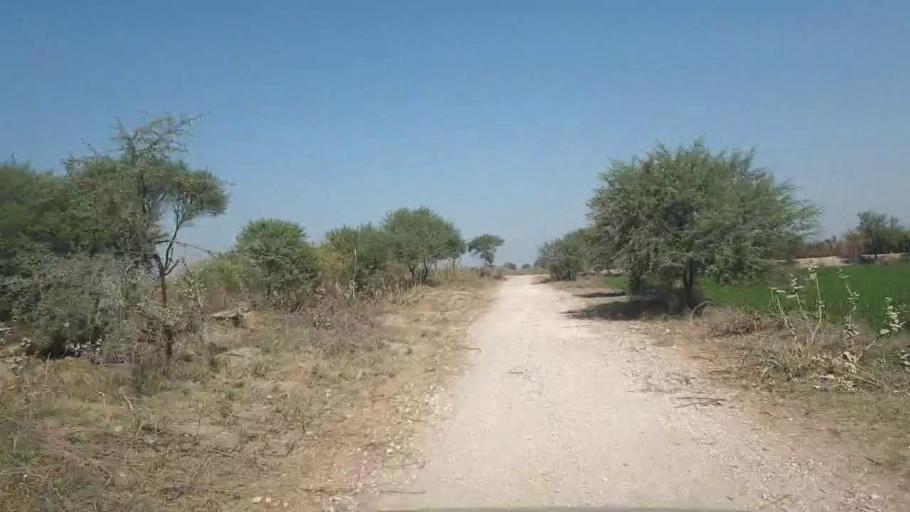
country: PK
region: Sindh
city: Chambar
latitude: 25.3086
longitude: 68.6967
